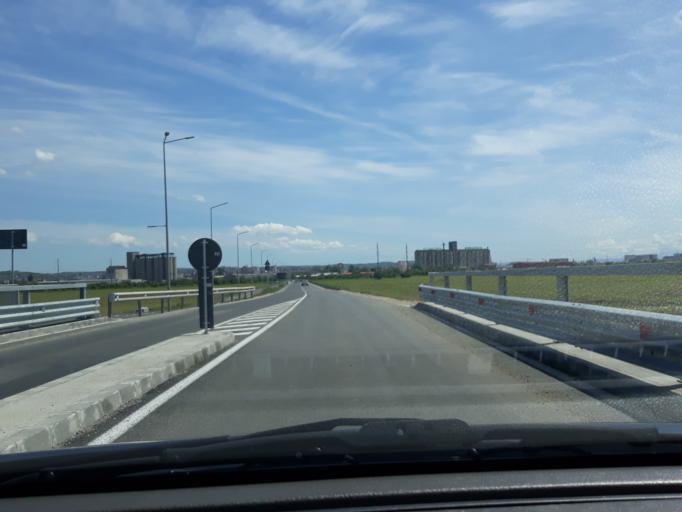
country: RO
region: Bihor
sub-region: Comuna Santandrei
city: Santandrei
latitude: 47.0667
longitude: 21.8776
